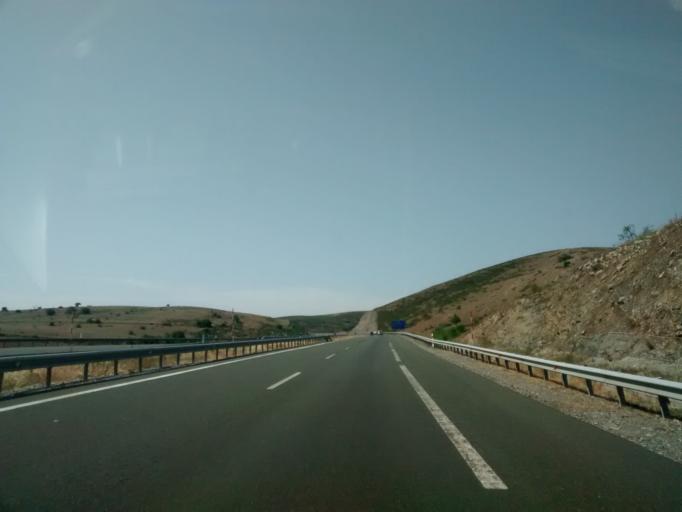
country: ES
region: Cantabria
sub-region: Provincia de Cantabria
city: Villaescusa
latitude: 42.9298
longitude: -4.1231
